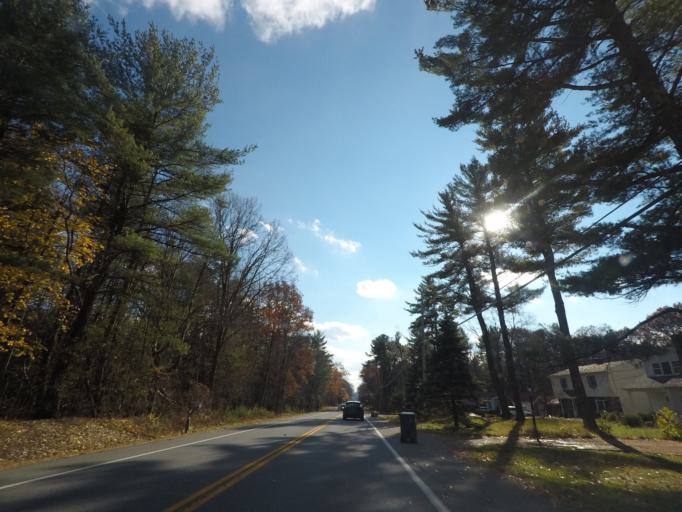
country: US
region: New York
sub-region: Schenectady County
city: East Glenville
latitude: 42.8718
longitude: -73.8877
